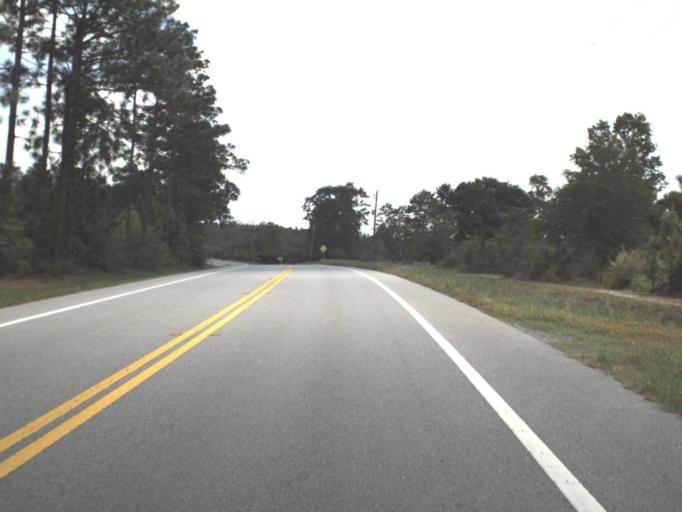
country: US
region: Florida
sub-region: Escambia County
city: Molino
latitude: 30.7988
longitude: -87.4230
